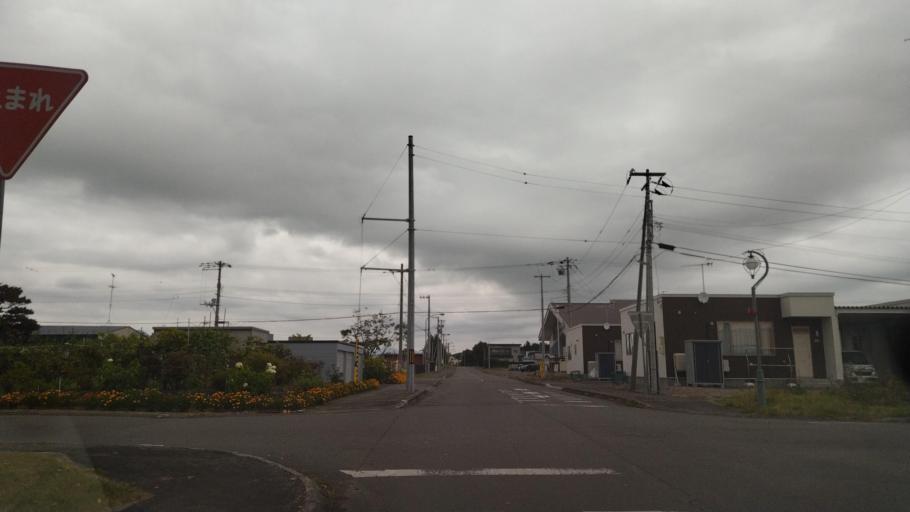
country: JP
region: Hokkaido
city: Otofuke
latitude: 43.2307
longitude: 143.2977
